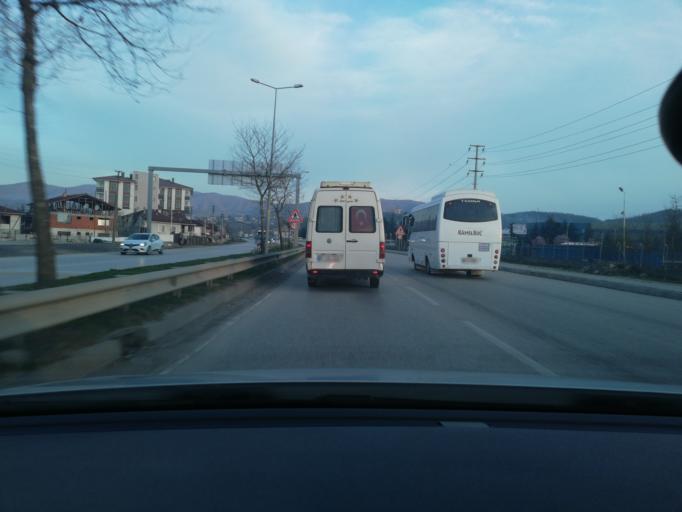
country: TR
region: Duzce
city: Konuralp
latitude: 40.8957
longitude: 31.1662
